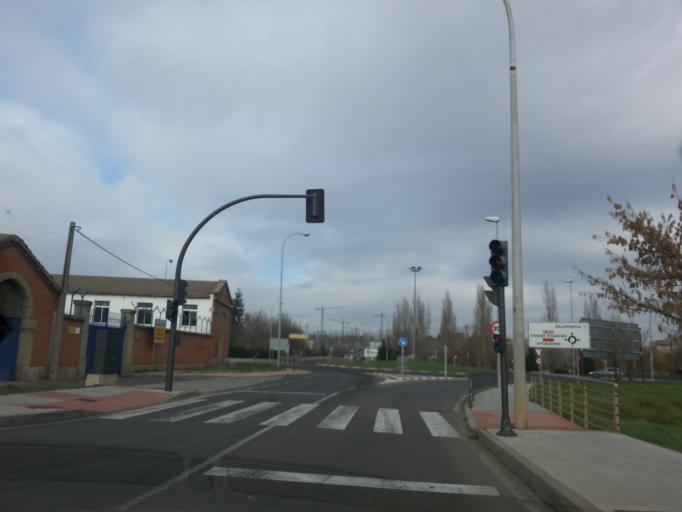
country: ES
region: Castille and Leon
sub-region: Provincia de Salamanca
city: Salamanca
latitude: 40.9544
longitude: -5.6763
